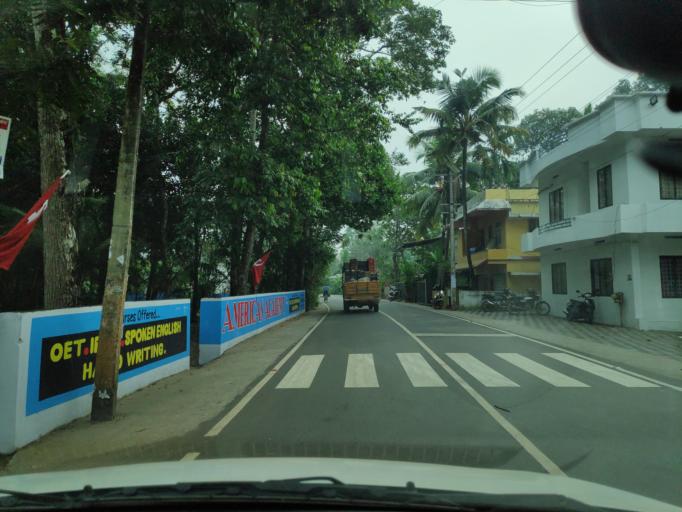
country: IN
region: Kerala
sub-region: Alappuzha
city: Shertallai
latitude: 9.6078
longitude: 76.3448
